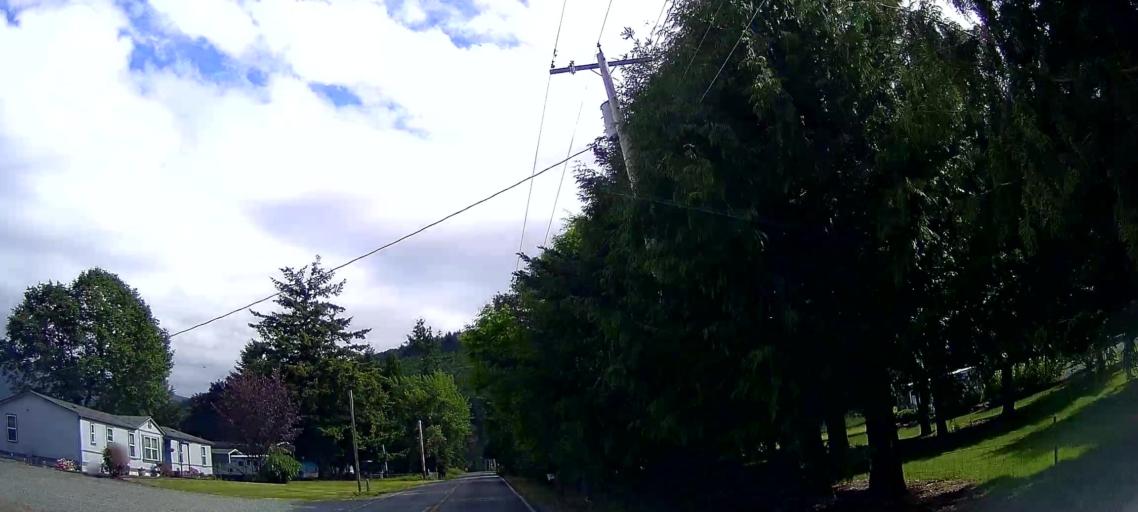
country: US
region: Washington
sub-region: Skagit County
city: Sedro-Woolley
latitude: 48.4954
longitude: -122.2093
